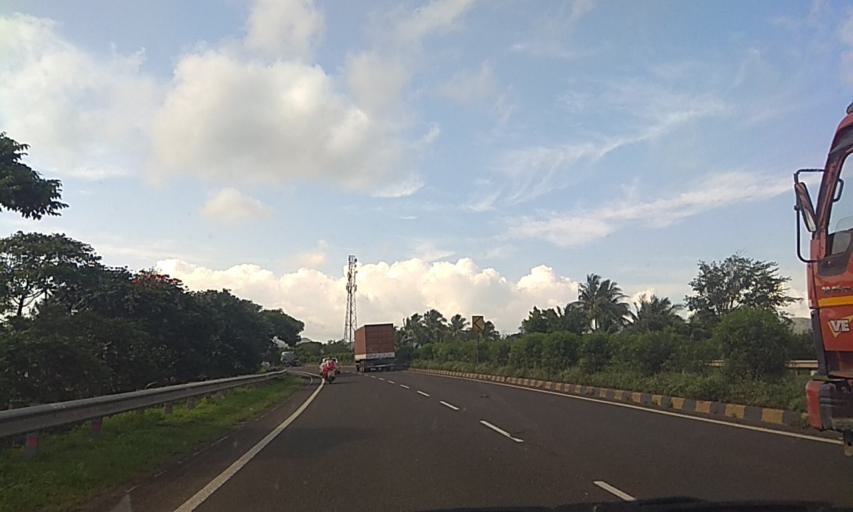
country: IN
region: Maharashtra
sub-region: Kolhapur
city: Kodoli
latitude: 16.9259
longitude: 74.2889
